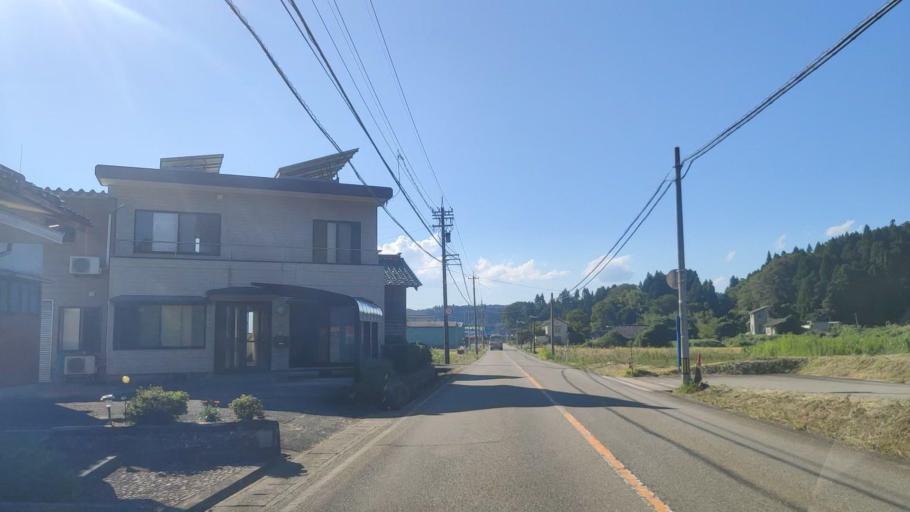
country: JP
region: Ishikawa
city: Nanao
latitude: 37.2343
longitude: 136.9707
